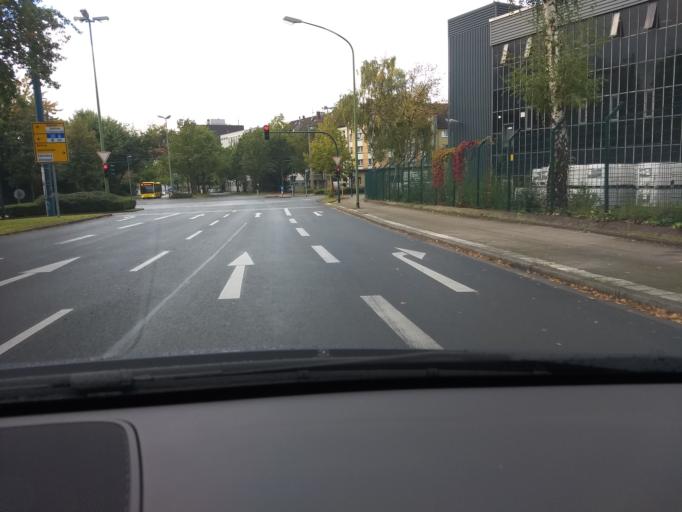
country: DE
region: North Rhine-Westphalia
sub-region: Regierungsbezirk Dusseldorf
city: Essen
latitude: 51.4616
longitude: 7.0207
